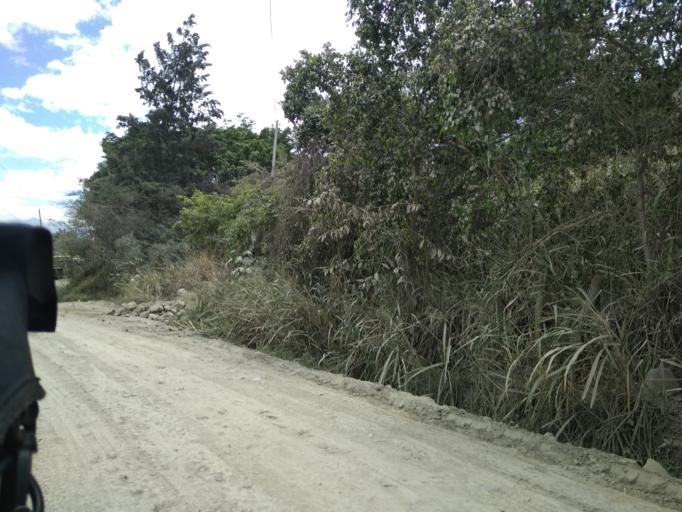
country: EC
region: Loja
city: Loja
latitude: -4.2122
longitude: -79.2392
